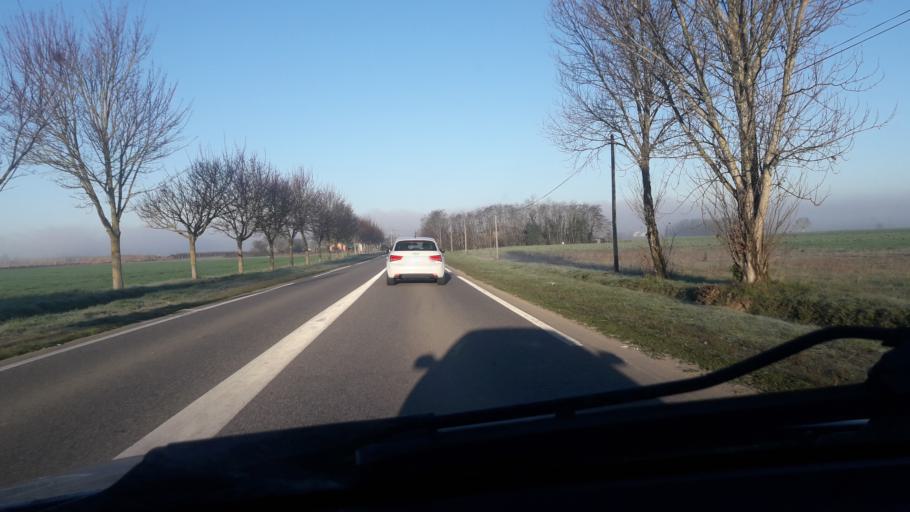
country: FR
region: Midi-Pyrenees
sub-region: Departement de la Haute-Garonne
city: Carbonne
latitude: 43.2972
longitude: 1.1999
